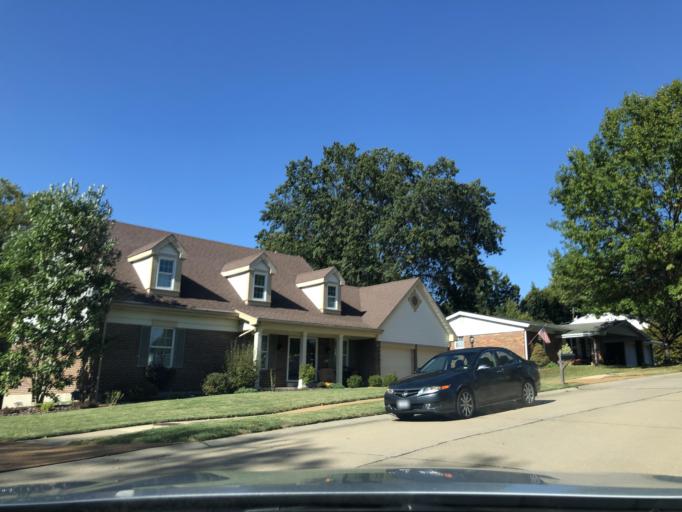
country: US
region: Missouri
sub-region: Saint Louis County
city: Concord
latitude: 38.5038
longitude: -90.3737
